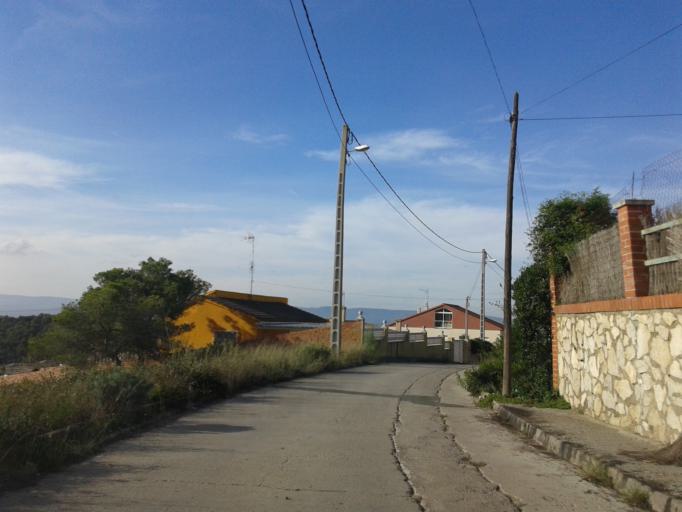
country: ES
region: Catalonia
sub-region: Provincia de Barcelona
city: Vilafranca del Penedes
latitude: 41.2938
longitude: 1.6993
